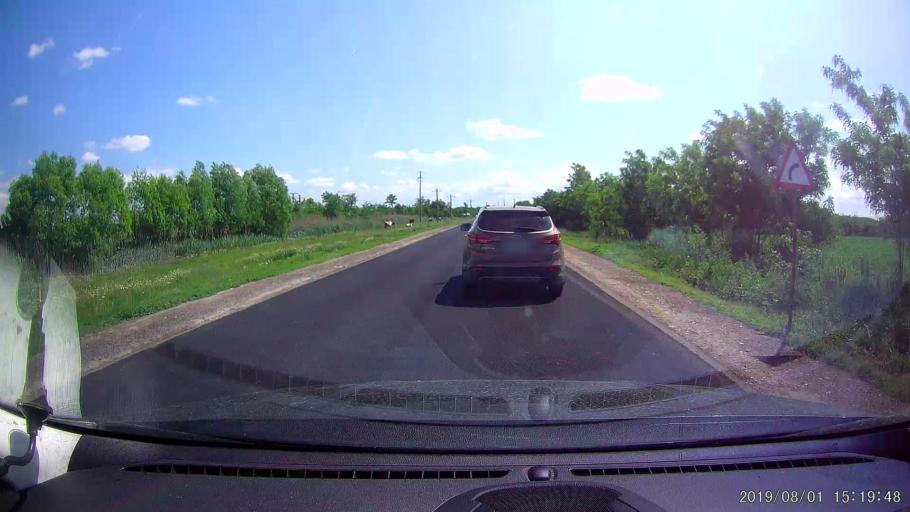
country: RO
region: Braila
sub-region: Comuna Unirea
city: Unirea
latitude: 45.0855
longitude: 27.8109
